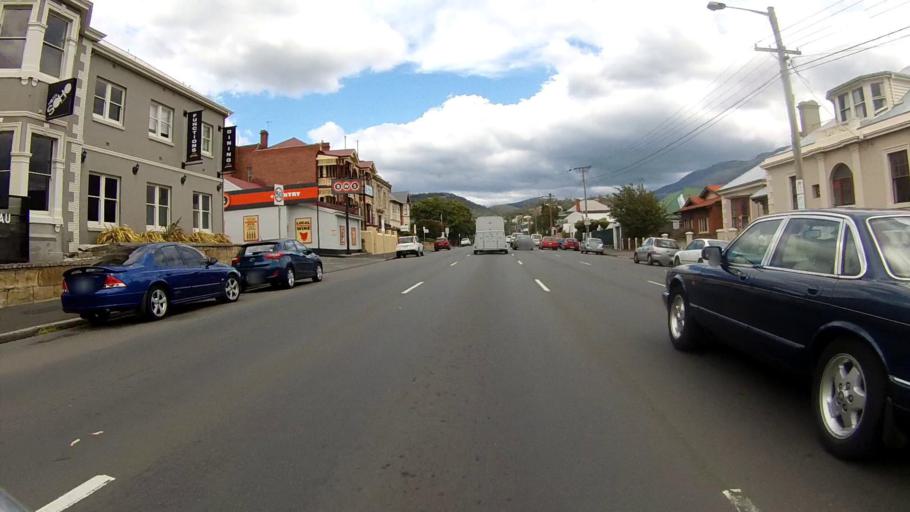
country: AU
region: Tasmania
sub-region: Hobart
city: Sandy Bay
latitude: -42.8894
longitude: 147.3234
